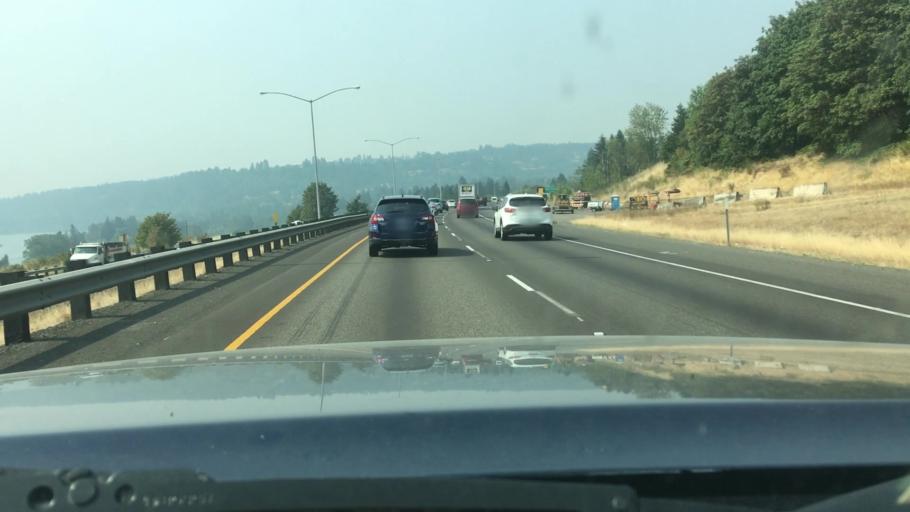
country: US
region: Oregon
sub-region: Clackamas County
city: West Linn
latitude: 45.3503
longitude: -122.6310
